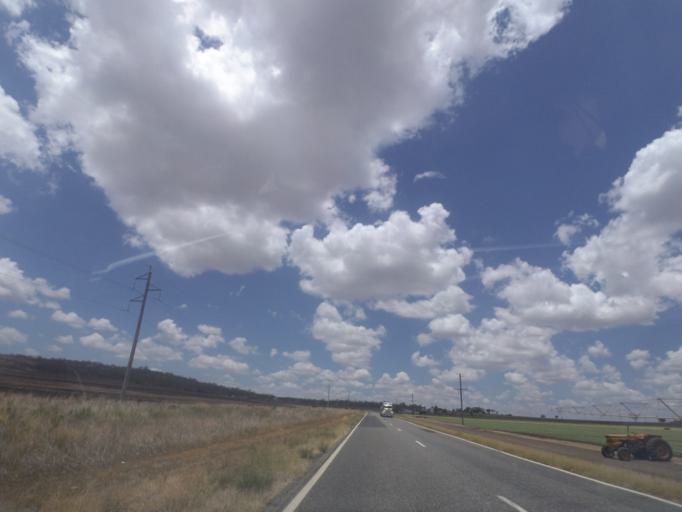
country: AU
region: Queensland
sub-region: Toowoomba
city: Top Camp
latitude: -27.8741
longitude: 151.9643
